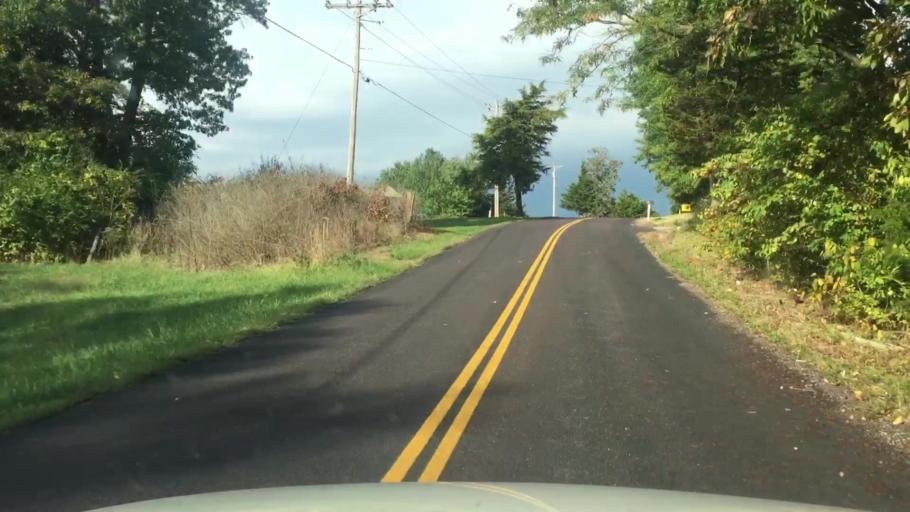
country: US
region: Missouri
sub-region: Boone County
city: Columbia
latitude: 38.8600
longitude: -92.3274
